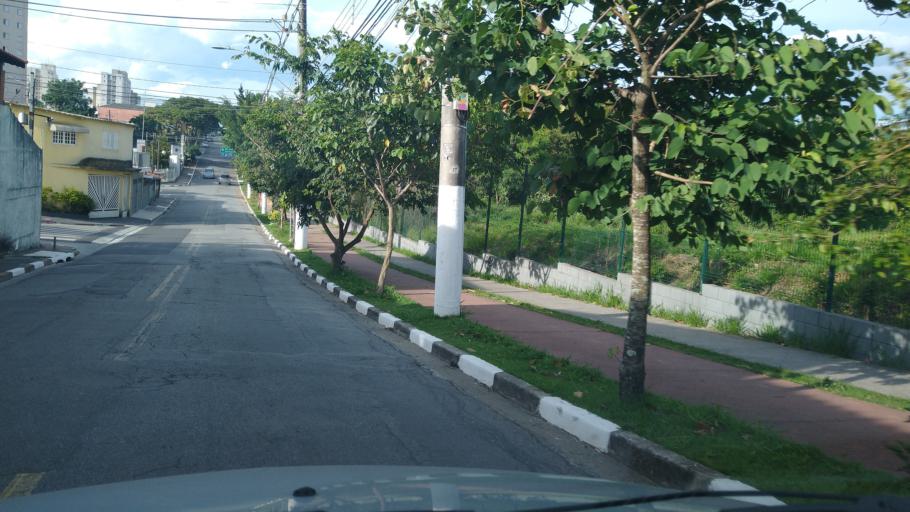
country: BR
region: Sao Paulo
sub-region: Osasco
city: Osasco
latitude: -23.5305
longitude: -46.8115
